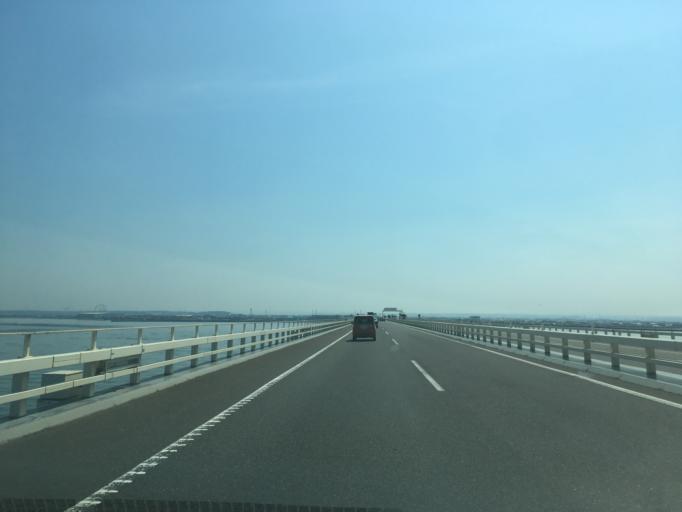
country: JP
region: Chiba
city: Kisarazu
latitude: 35.4456
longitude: 139.9021
